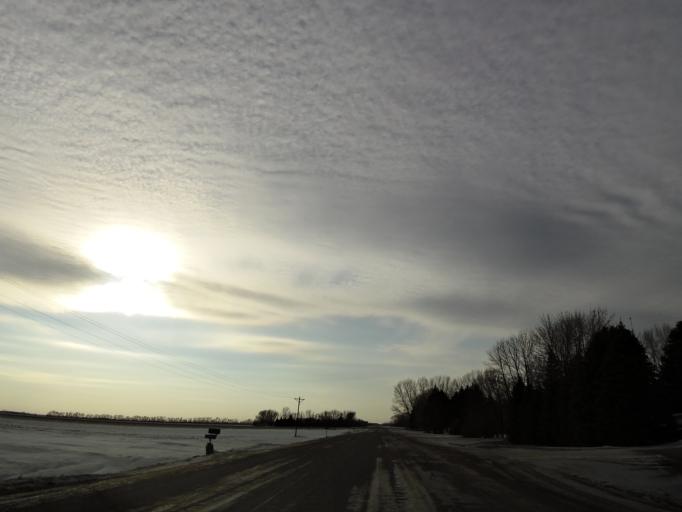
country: US
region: North Dakota
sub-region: Walsh County
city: Grafton
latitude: 48.4270
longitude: -97.3169
